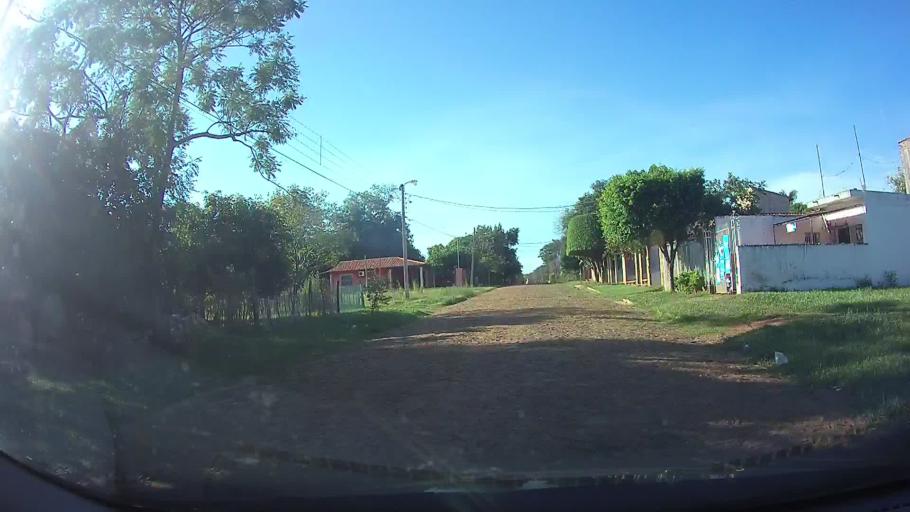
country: PY
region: Central
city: Limpio
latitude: -25.2549
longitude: -57.4684
